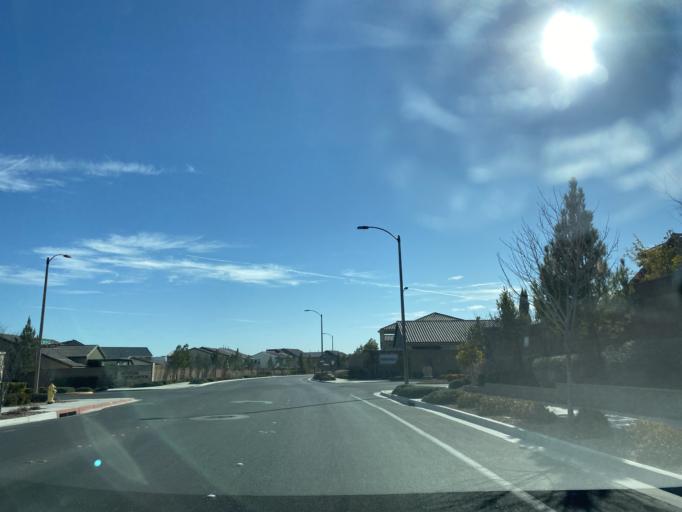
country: US
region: Nevada
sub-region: Clark County
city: Summerlin South
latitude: 36.3133
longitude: -115.3105
